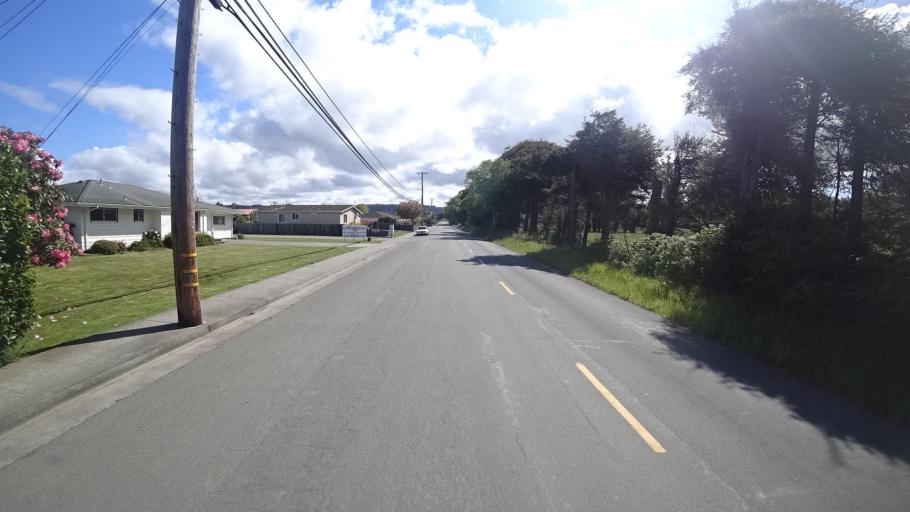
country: US
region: California
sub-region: Humboldt County
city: McKinleyville
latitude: 40.9445
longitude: -124.1095
